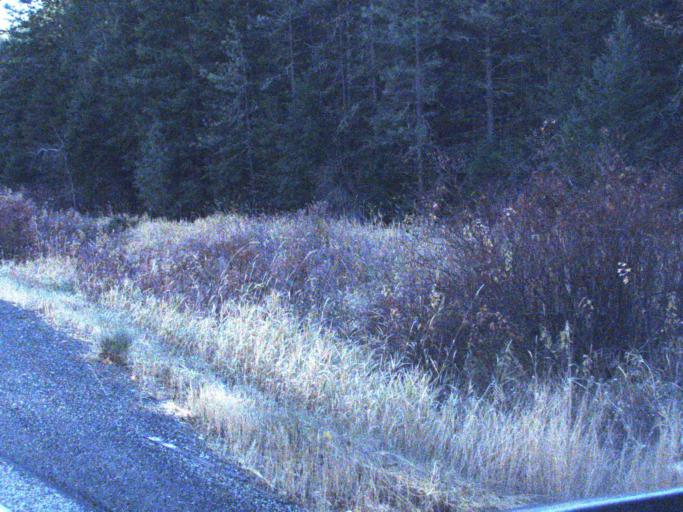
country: US
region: Washington
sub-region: Ferry County
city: Republic
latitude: 48.7786
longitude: -118.6333
